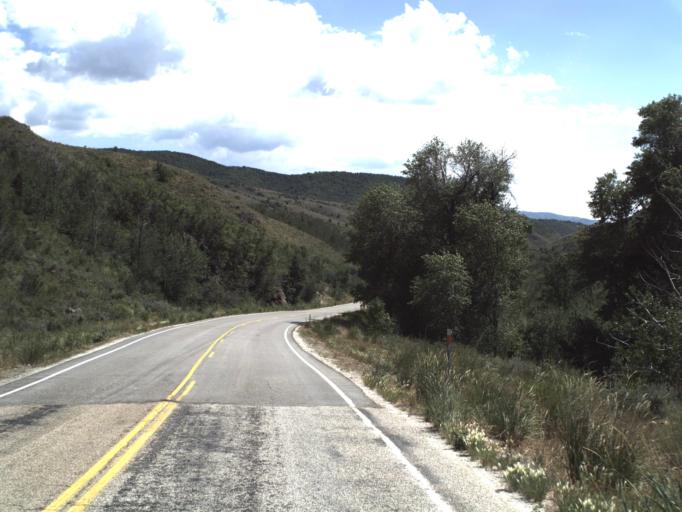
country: US
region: Utah
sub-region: Weber County
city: Wolf Creek
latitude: 41.3642
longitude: -111.5917
